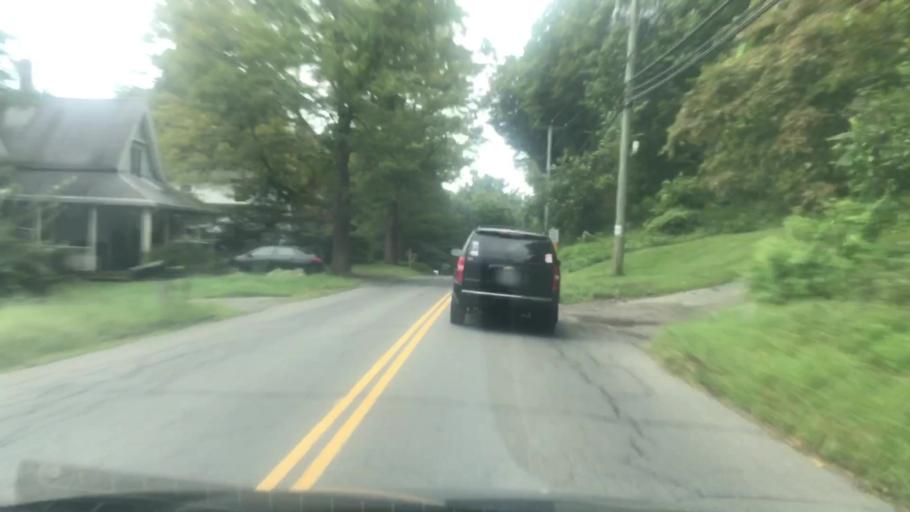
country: US
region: Connecticut
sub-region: Litchfield County
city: New Milford
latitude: 41.6023
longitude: -73.4173
